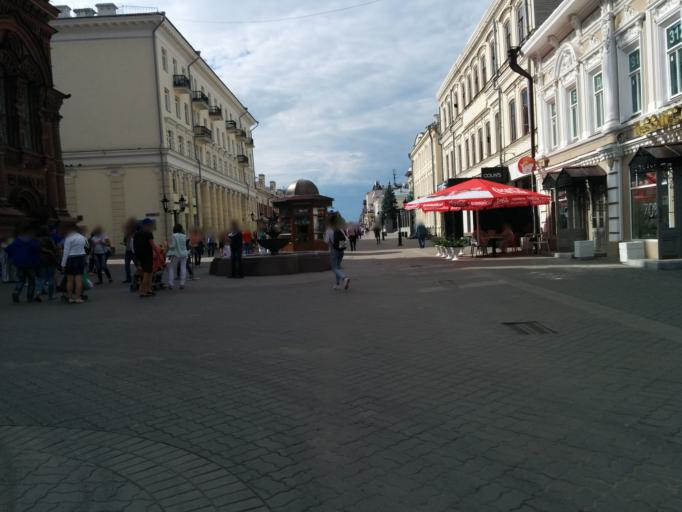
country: RU
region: Tatarstan
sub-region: Gorod Kazan'
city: Kazan
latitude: 55.7883
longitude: 49.1198
